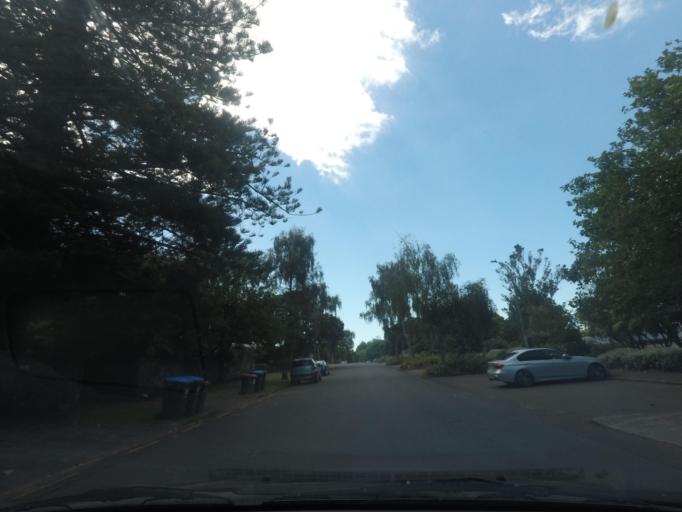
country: NZ
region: Auckland
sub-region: Auckland
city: Auckland
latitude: -36.8872
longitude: 174.7673
